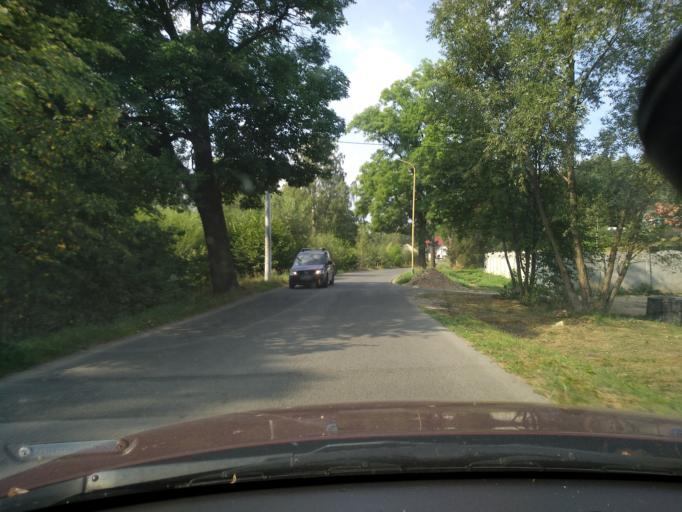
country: PL
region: Lower Silesian Voivodeship
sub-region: Powiat jeleniogorski
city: Stara Kamienica
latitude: 50.9284
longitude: 15.5772
